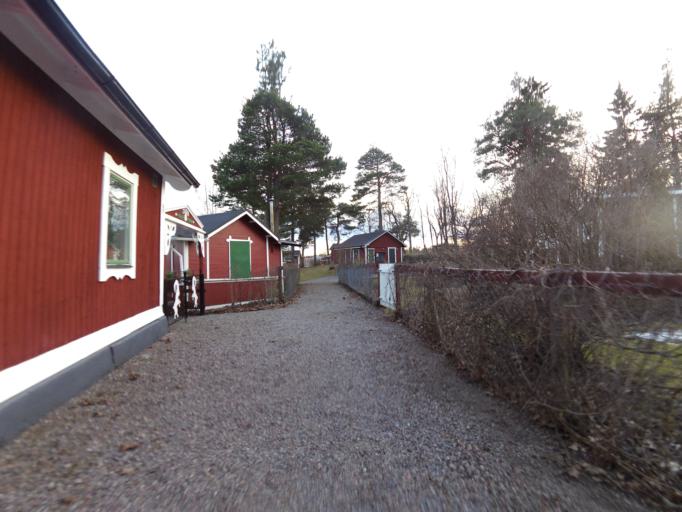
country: SE
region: Gaevleborg
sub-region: Gavle Kommun
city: Gavle
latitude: 60.6642
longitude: 17.1614
